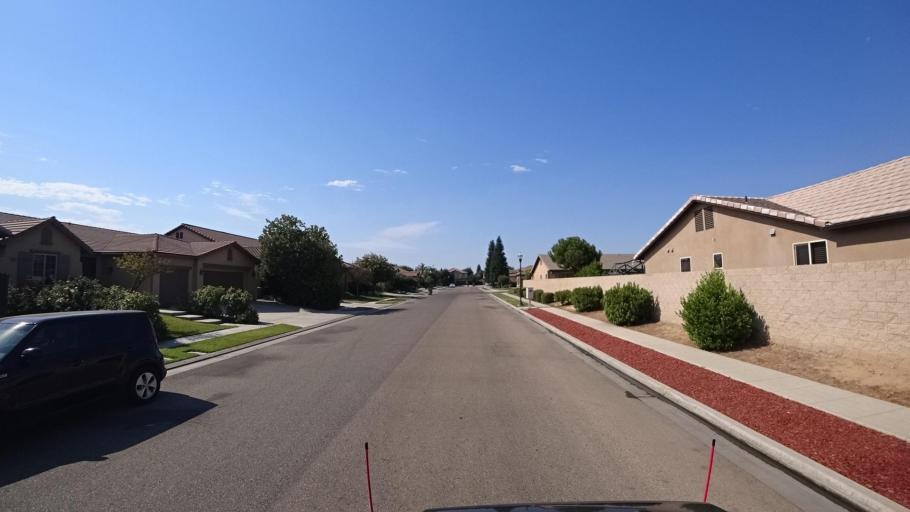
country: US
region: California
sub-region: Fresno County
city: Sunnyside
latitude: 36.7133
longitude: -119.6848
